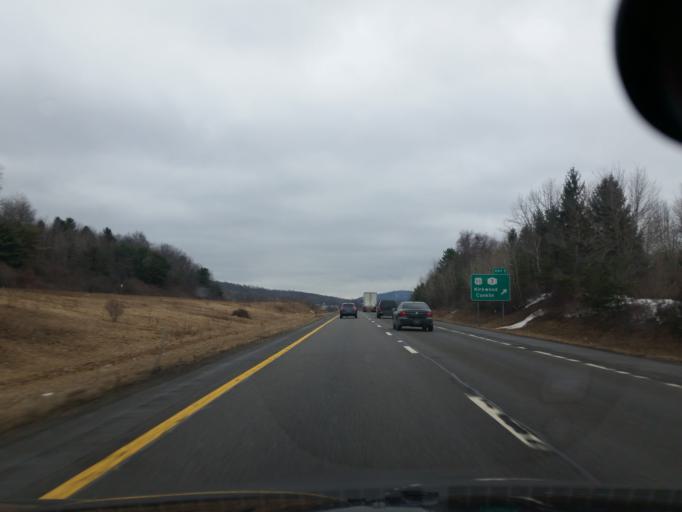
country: US
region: Pennsylvania
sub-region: Susquehanna County
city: Hallstead
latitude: 42.0478
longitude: -75.7959
